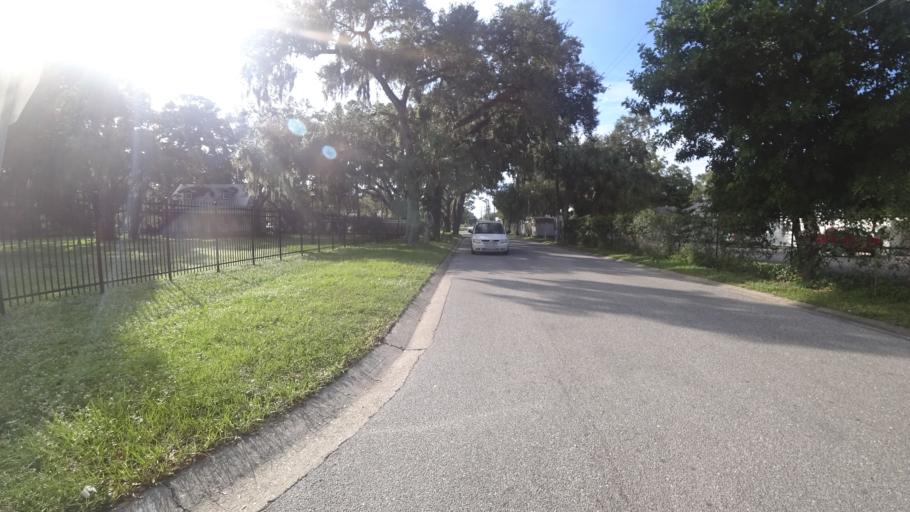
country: US
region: Florida
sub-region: Manatee County
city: Samoset
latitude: 27.4938
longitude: -82.5485
